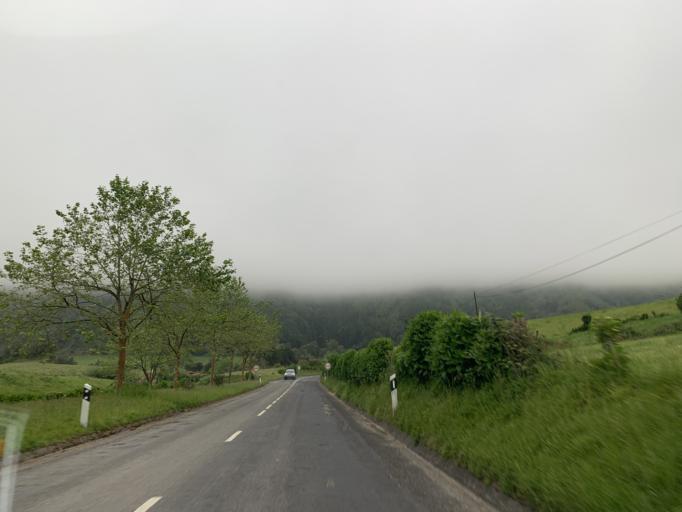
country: PT
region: Azores
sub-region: Ponta Delgada
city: Arrifes
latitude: 37.8622
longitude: -25.8056
